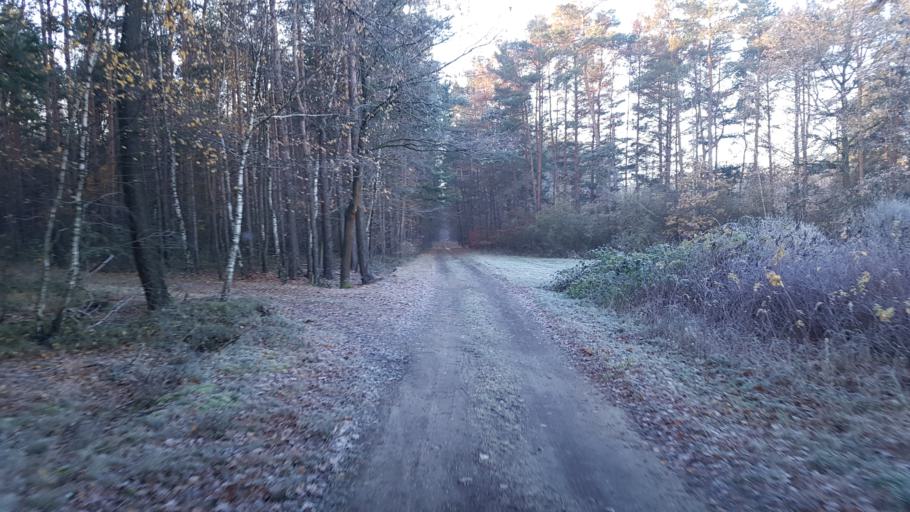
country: DE
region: Brandenburg
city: Sallgast
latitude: 51.6052
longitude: 13.8354
